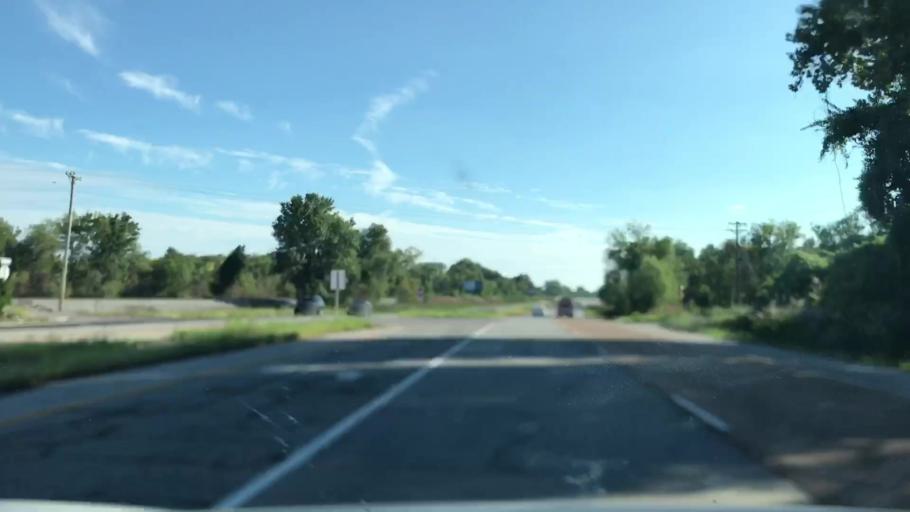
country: US
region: Illinois
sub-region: Madison County
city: Hartford
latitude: 38.7970
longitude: -90.1018
